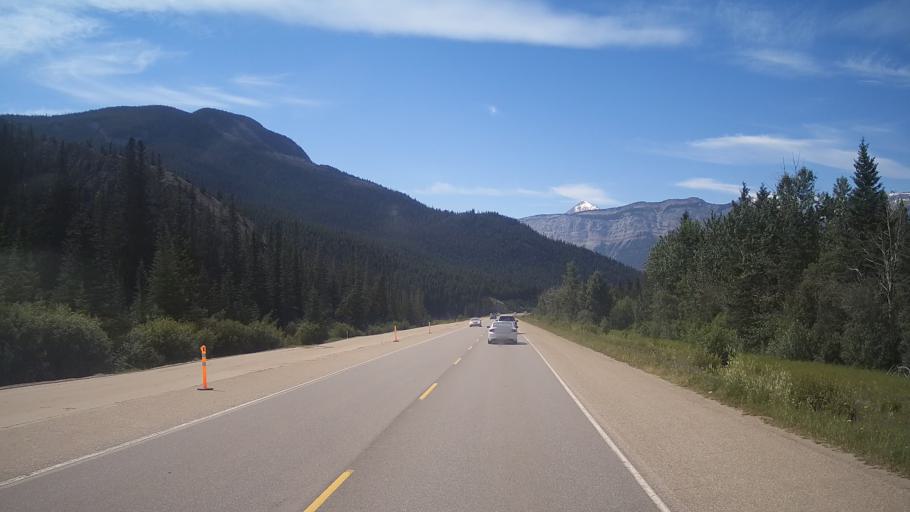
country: CA
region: Alberta
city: Jasper Park Lodge
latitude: 53.0585
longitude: -118.0681
